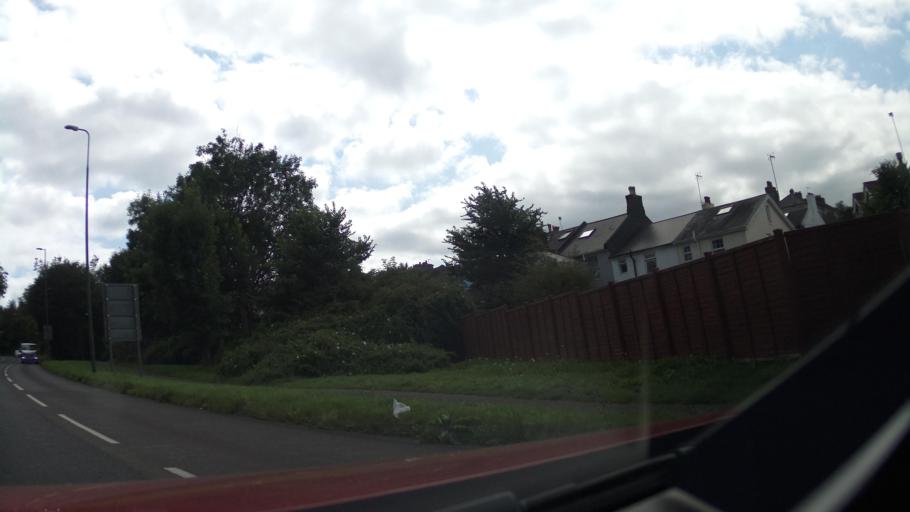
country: GB
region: England
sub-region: Borough of Torbay
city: Torquay
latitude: 50.4884
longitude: -3.5259
